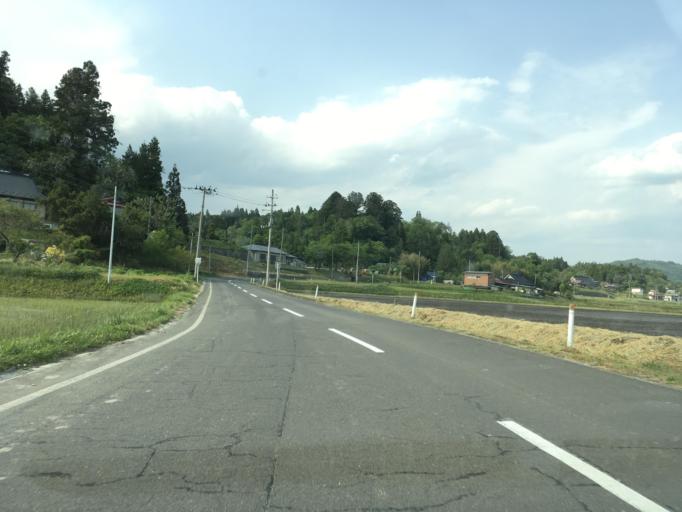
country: JP
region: Iwate
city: Ichinoseki
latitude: 38.9502
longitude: 141.3501
